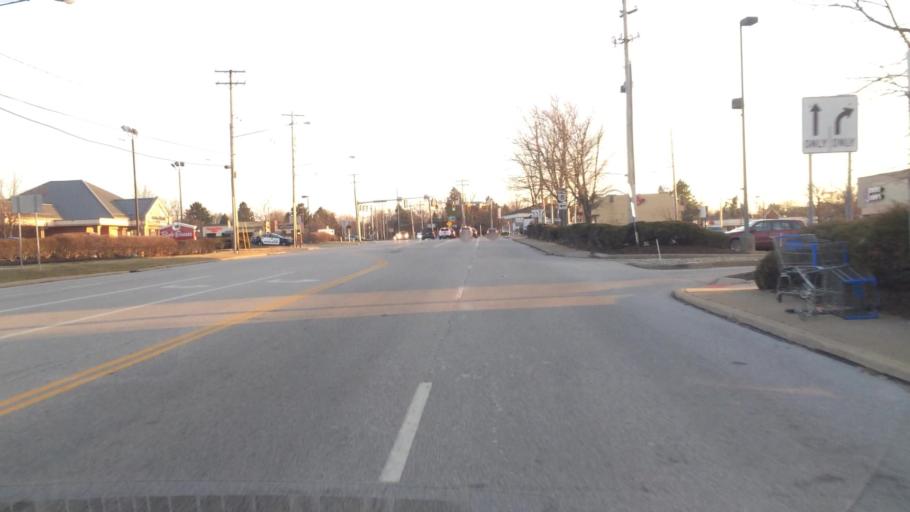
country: US
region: Ohio
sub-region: Summit County
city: Silver Lake
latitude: 41.1650
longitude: -81.4771
